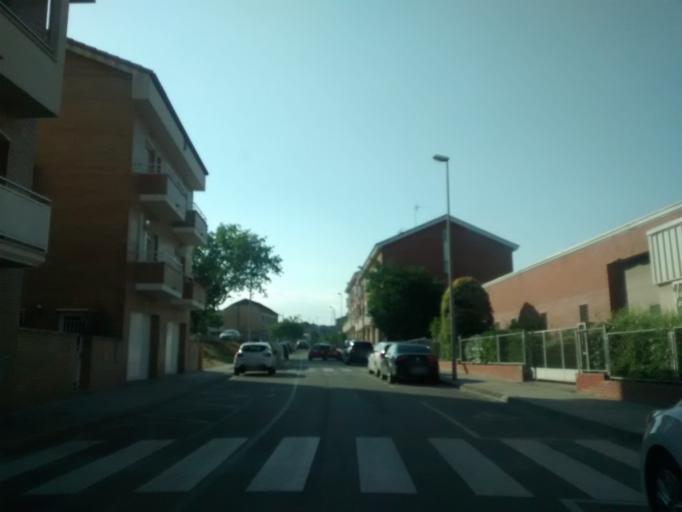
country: ES
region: Catalonia
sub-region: Provincia de Barcelona
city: Sant Vicenc dels Horts
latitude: 41.3874
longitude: 2.0136
